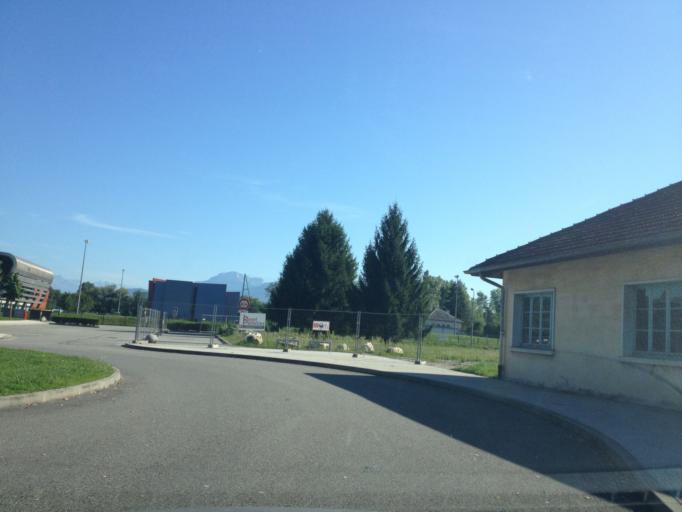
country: FR
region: Rhone-Alpes
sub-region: Departement de la Savoie
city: Le Bourget-du-Lac
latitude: 45.6406
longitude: 5.8712
